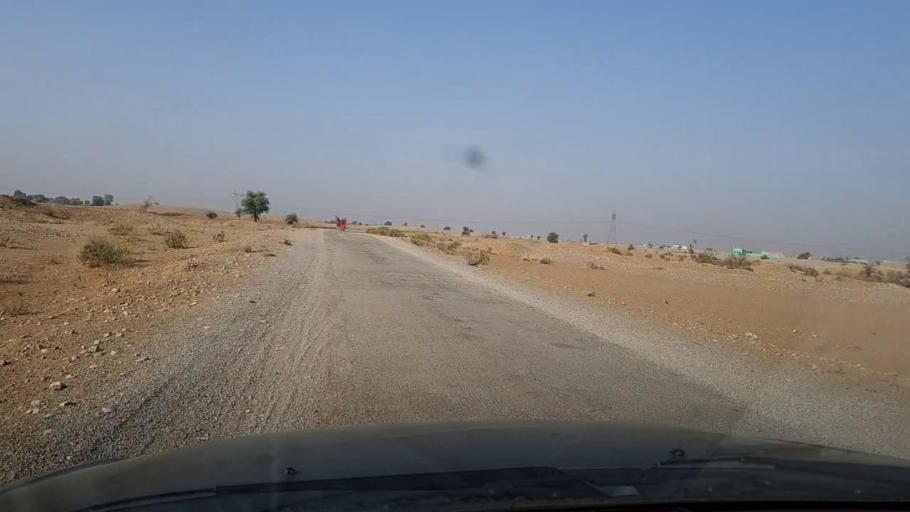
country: PK
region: Sindh
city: Sann
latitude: 26.0125
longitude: 68.0936
